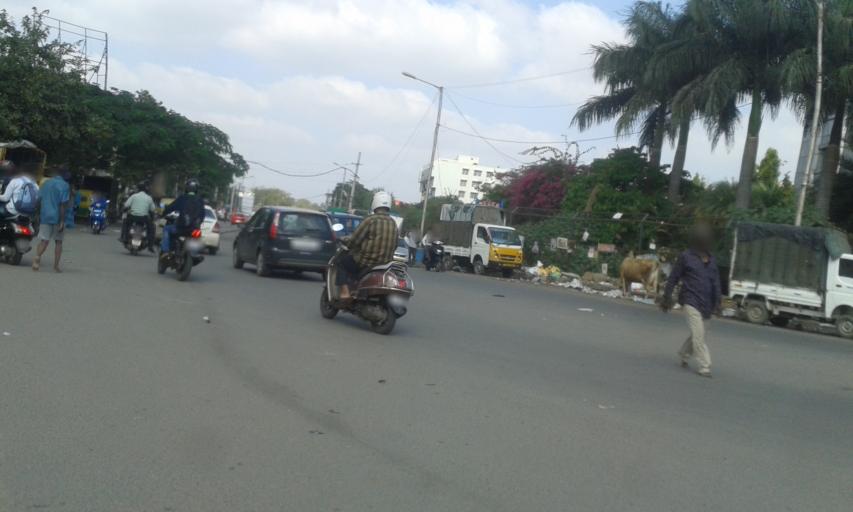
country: IN
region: Karnataka
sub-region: Bangalore Urban
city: Bangalore
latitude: 12.9459
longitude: 77.6185
